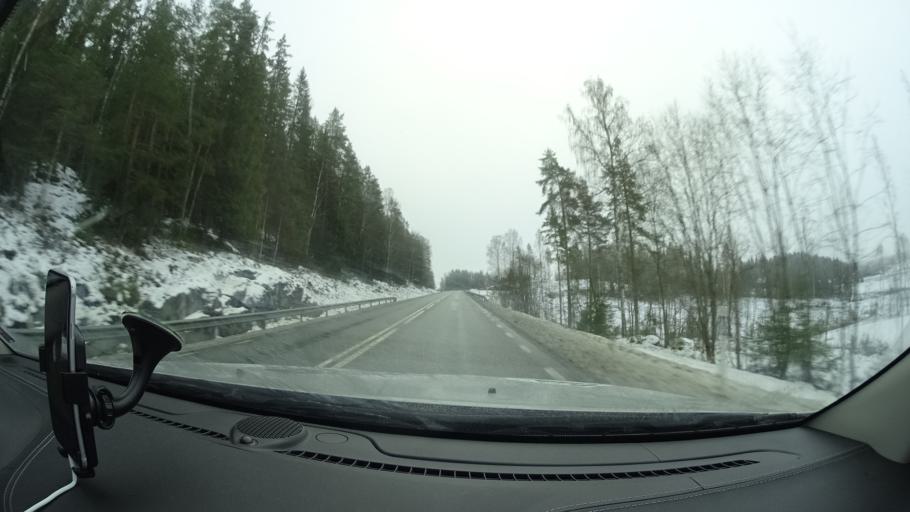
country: SE
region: OErebro
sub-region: Lindesbergs Kommun
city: Stora
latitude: 59.8267
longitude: 15.1146
